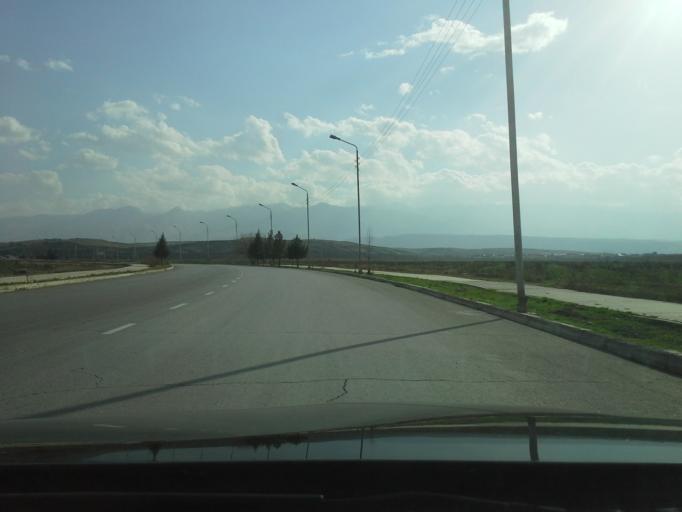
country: TM
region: Ahal
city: Ashgabat
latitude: 37.9846
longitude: 58.2820
